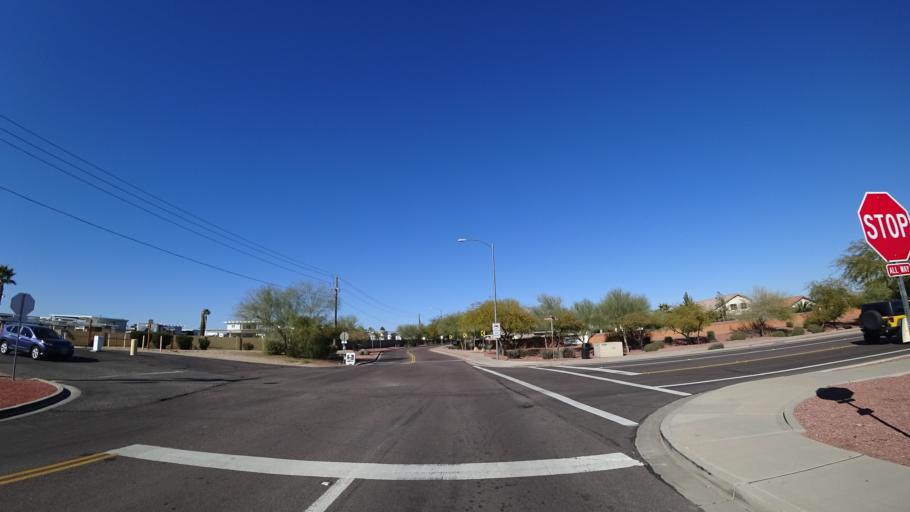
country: US
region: Arizona
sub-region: Maricopa County
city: Sun City West
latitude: 33.6493
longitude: -112.4267
